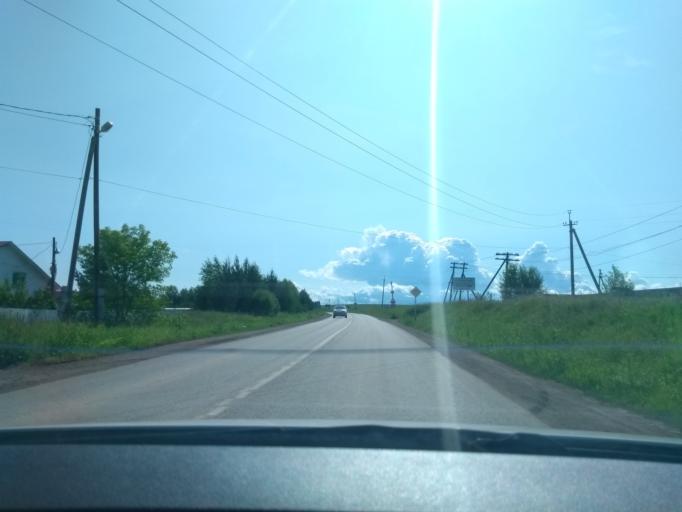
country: RU
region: Perm
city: Lobanovo
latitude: 57.8564
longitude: 56.3104
